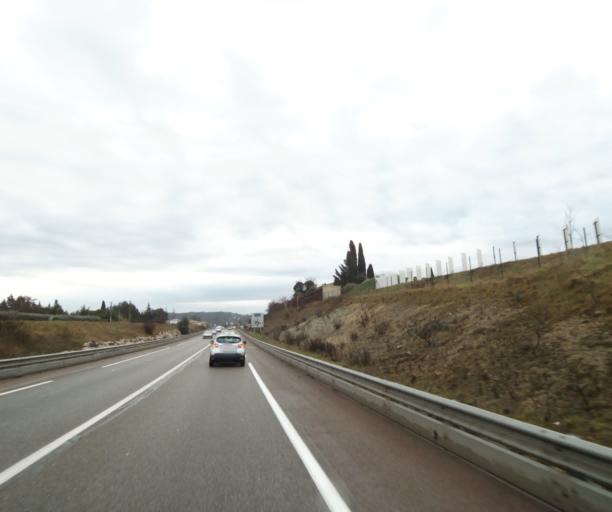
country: FR
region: Provence-Alpes-Cote d'Azur
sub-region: Departement du Var
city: Brignoles
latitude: 43.4150
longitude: 6.0657
